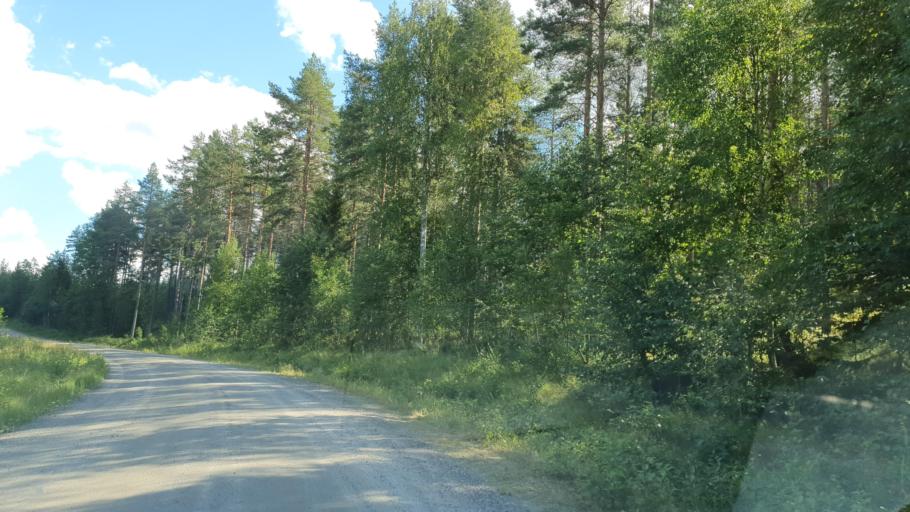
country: FI
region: Kainuu
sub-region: Kehys-Kainuu
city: Kuhmo
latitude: 64.0990
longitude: 29.4051
